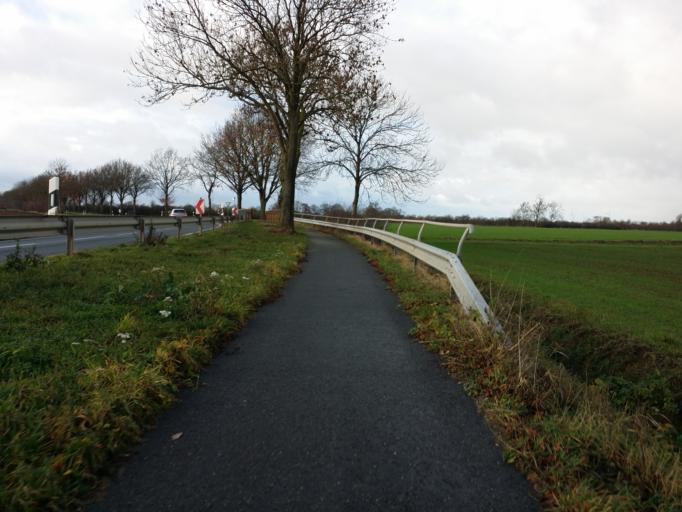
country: DE
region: Lower Saxony
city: Riede
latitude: 52.9890
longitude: 8.9758
